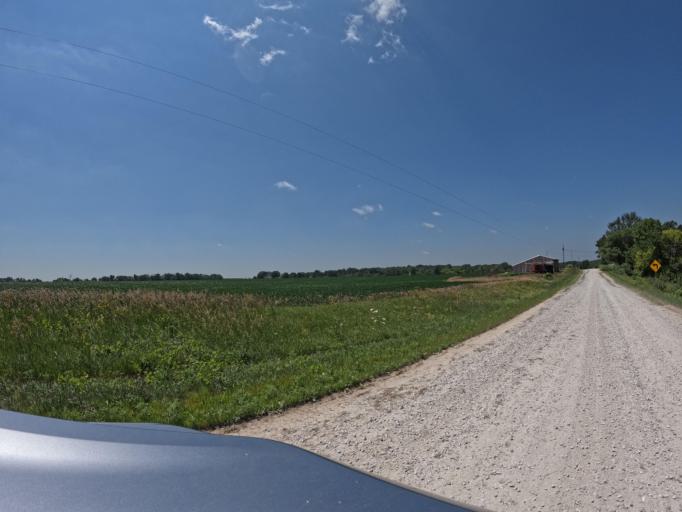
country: US
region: Iowa
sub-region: Keokuk County
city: Sigourney
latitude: 41.2885
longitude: -92.2346
